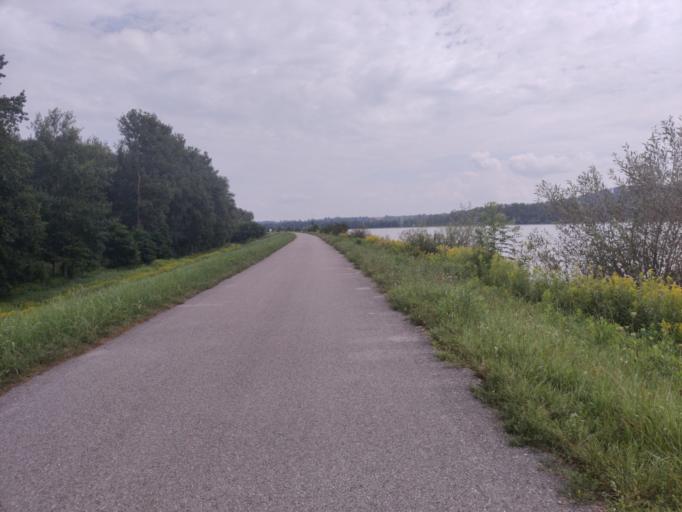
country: AT
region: Lower Austria
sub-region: Politischer Bezirk Amstetten
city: Strengberg
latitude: 48.1694
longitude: 14.6599
